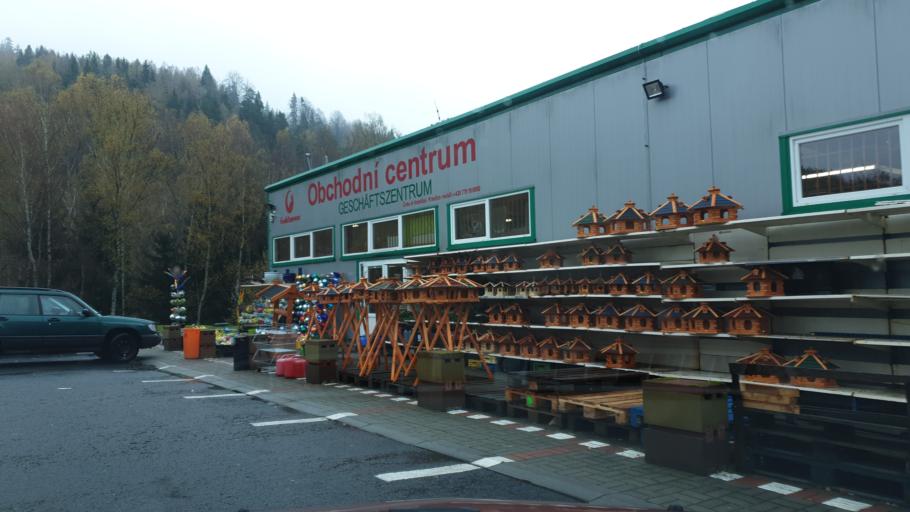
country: DE
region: Saxony
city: Klingenthal
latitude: 50.3499
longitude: 12.4755
